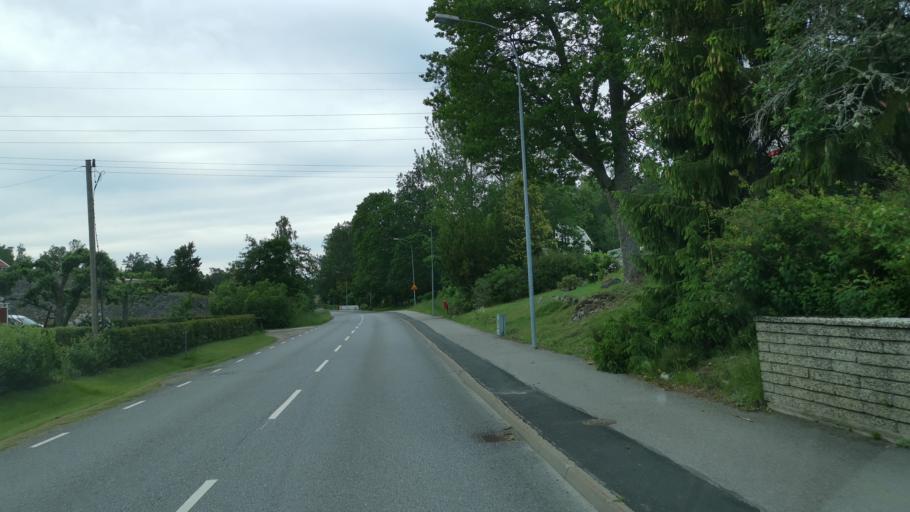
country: SE
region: Vaestra Goetaland
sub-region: Vanersborgs Kommun
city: Vargon
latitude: 58.3484
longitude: 12.3525
